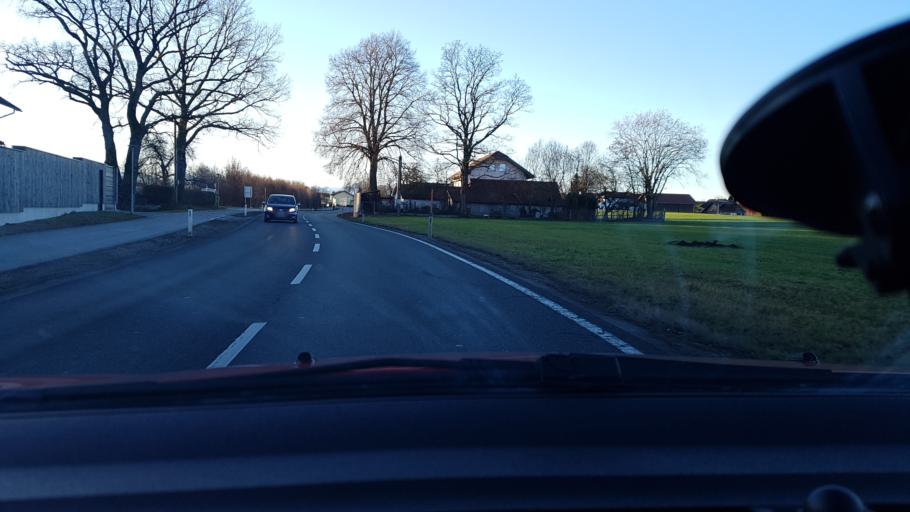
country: AT
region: Salzburg
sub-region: Politischer Bezirk Salzburg-Umgebung
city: Lamprechtshausen
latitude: 48.0014
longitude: 12.9581
